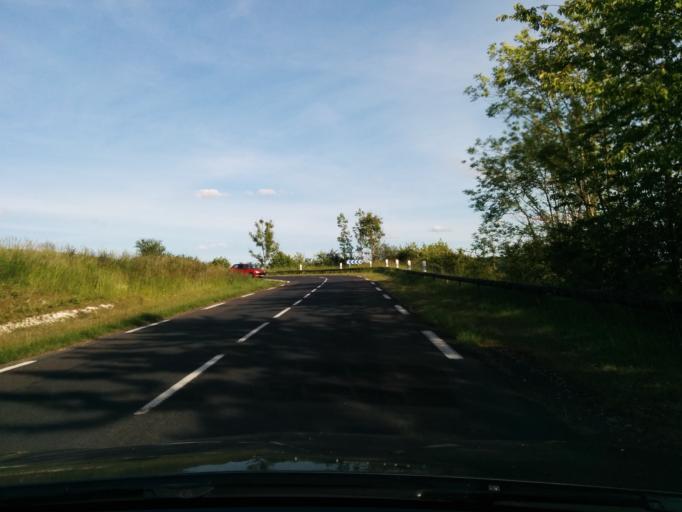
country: FR
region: Haute-Normandie
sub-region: Departement de l'Eure
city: Charleval
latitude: 49.3512
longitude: 1.4624
